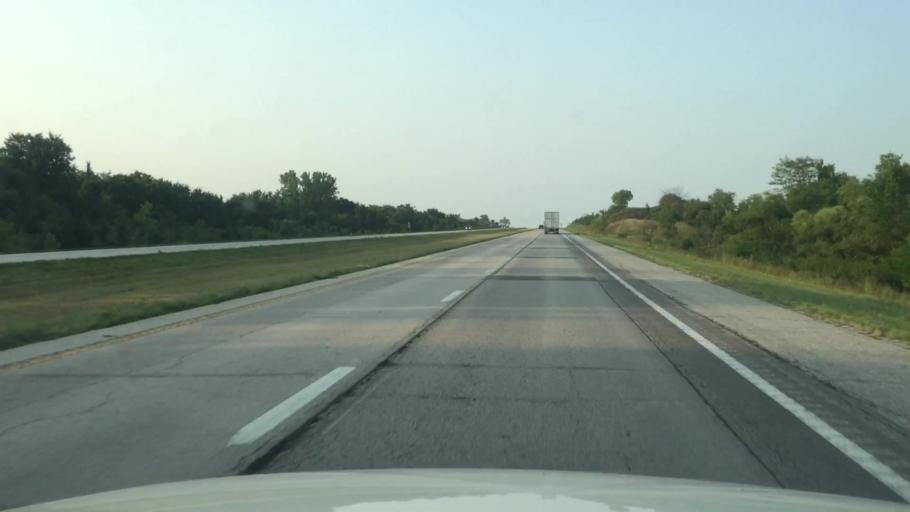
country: US
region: Iowa
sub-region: Decatur County
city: Lamoni
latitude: 40.4830
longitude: -93.9720
